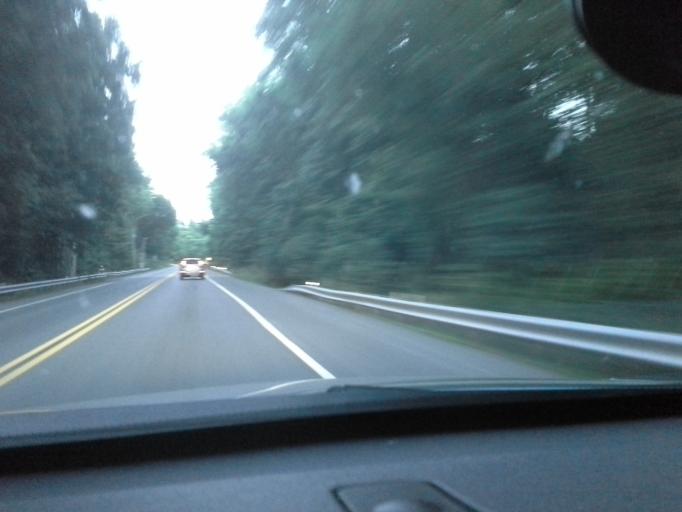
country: US
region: Maryland
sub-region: Calvert County
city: Huntingtown
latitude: 38.5976
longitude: -76.5860
